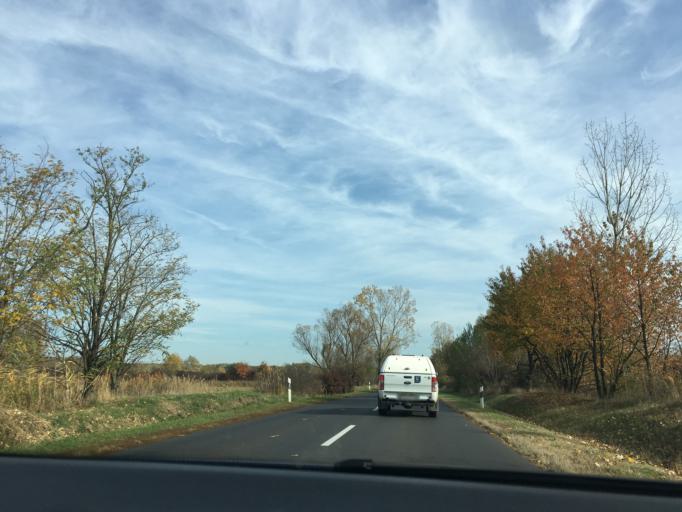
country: HU
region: Szabolcs-Szatmar-Bereg
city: Kisleta
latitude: 47.8546
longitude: 21.9941
